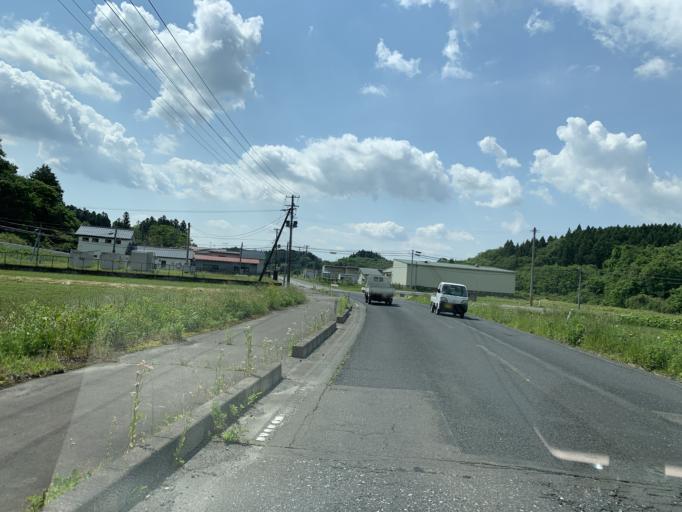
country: JP
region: Miyagi
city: Furukawa
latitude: 38.6973
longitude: 140.9277
